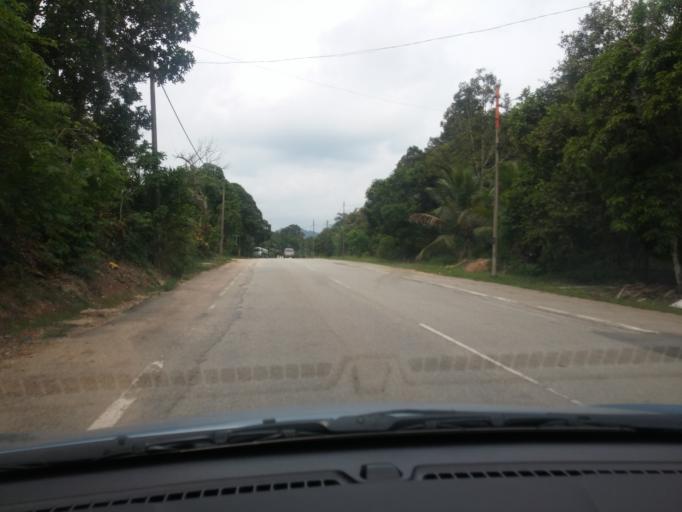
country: MY
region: Pahang
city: Kuantan
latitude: 3.8837
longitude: 103.1629
